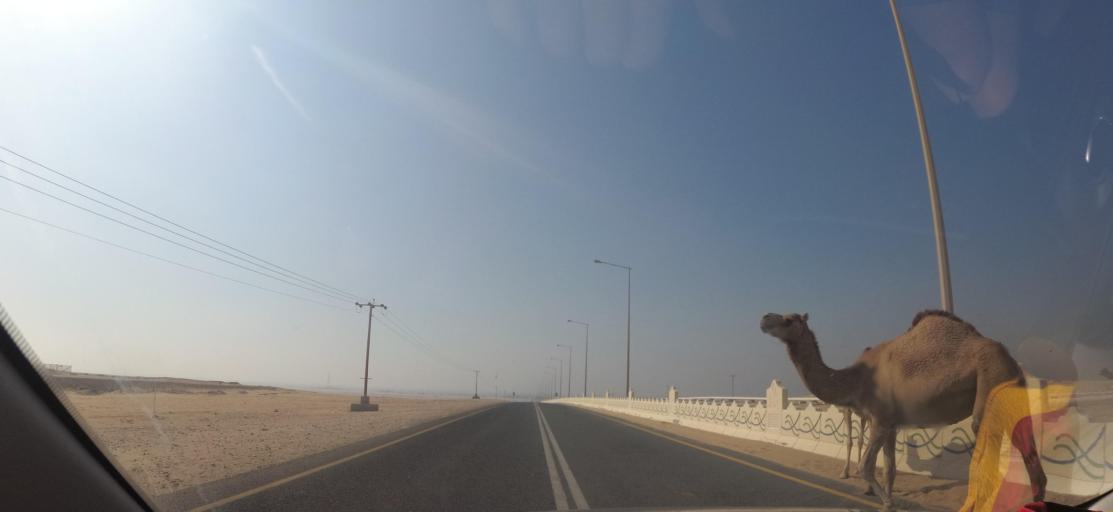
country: QA
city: Umm Bab
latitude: 25.2117
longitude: 50.7898
